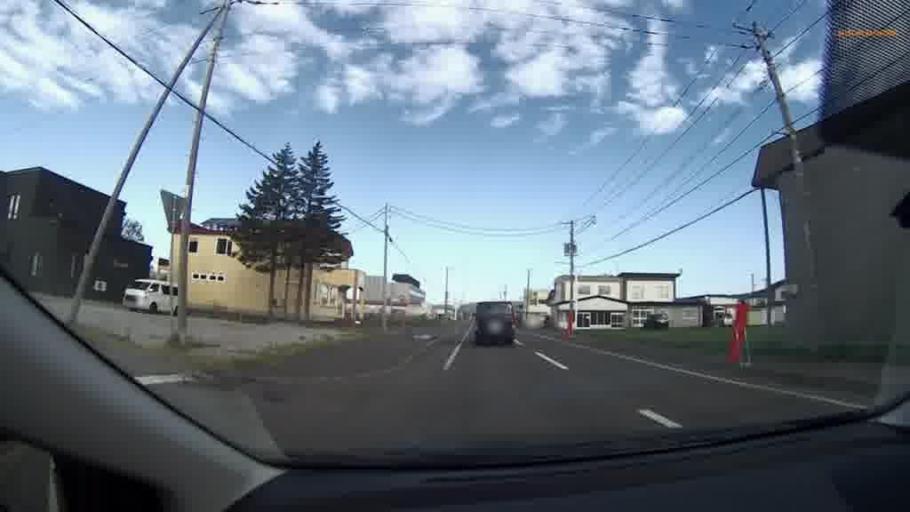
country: JP
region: Hokkaido
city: Kushiro
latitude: 42.9596
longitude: 144.0735
